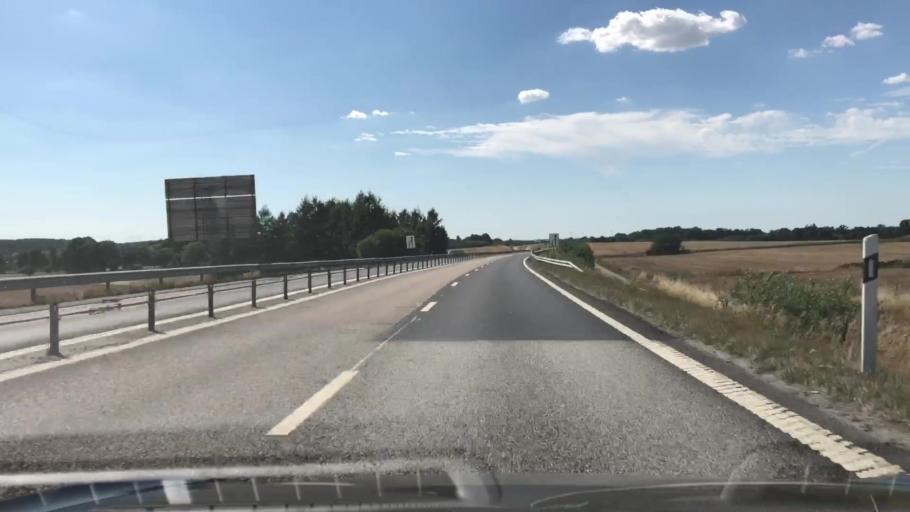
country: SE
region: Skane
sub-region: Horby Kommun
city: Hoerby
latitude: 55.8525
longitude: 13.6229
